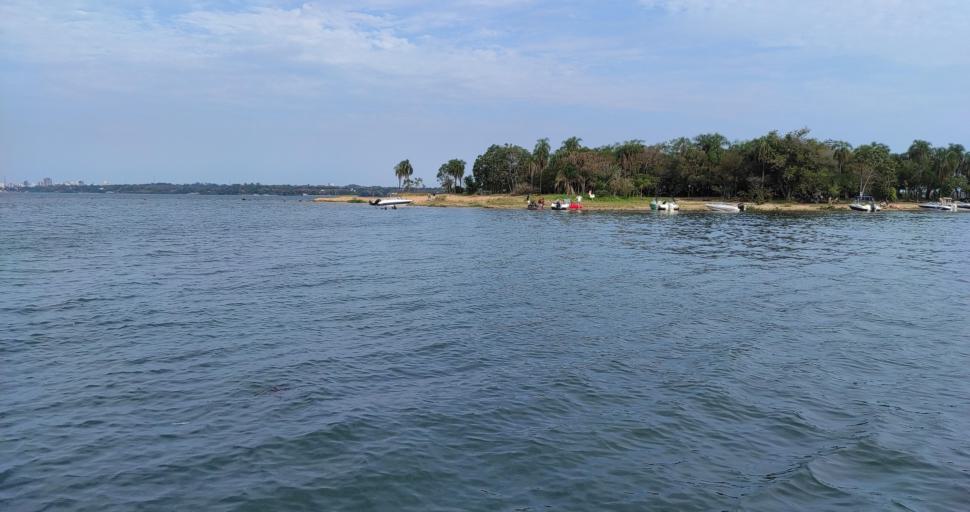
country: PY
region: Itapua
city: San Juan del Parana
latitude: -27.3388
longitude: -55.9509
